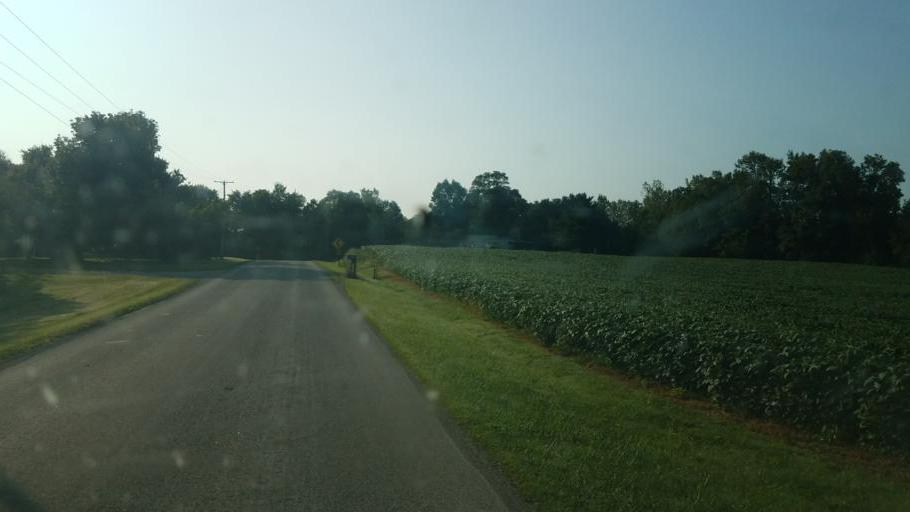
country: US
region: Ohio
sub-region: Morrow County
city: Mount Gilead
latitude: 40.5642
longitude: -82.6960
